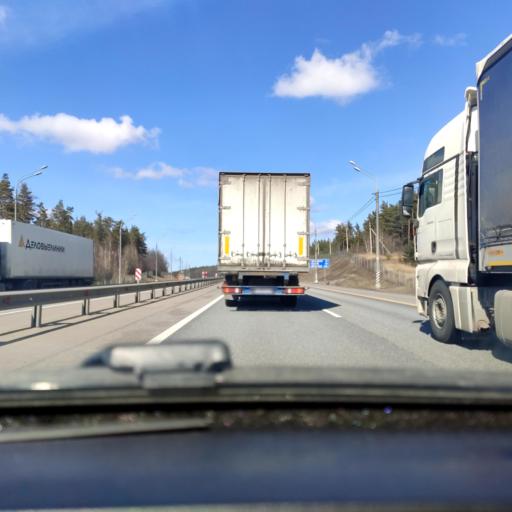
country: RU
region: Lipetsk
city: Khlevnoye
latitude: 52.2961
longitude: 39.0519
